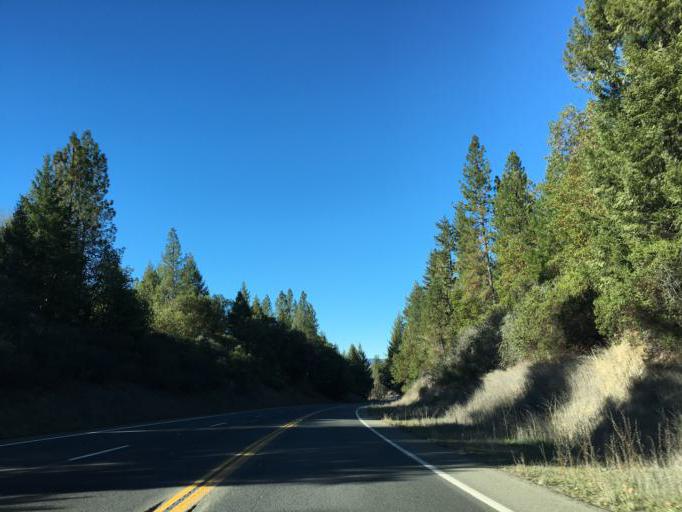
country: US
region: California
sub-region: Mendocino County
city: Laytonville
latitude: 39.7159
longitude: -123.4990
